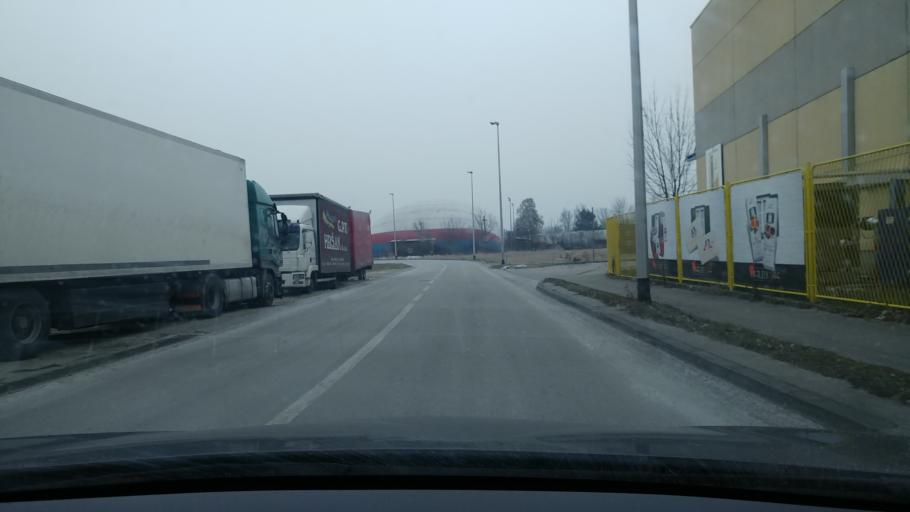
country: HR
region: Grad Zagreb
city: Stenjevec
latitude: 45.8114
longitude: 15.8840
